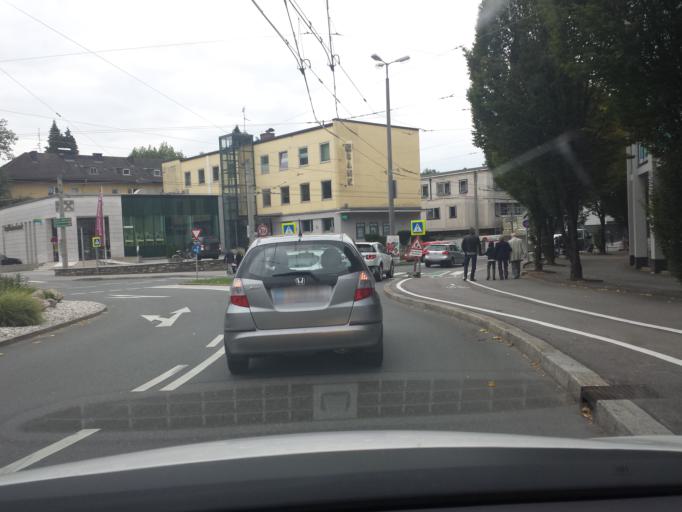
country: AT
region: Salzburg
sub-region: Salzburg Stadt
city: Salzburg
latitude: 47.8019
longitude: 13.0670
